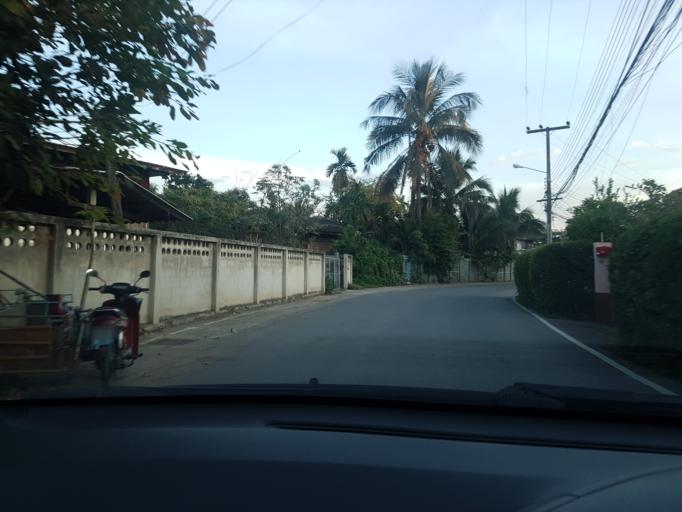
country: TH
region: Chiang Mai
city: San Sai
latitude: 18.8341
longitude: 99.0444
